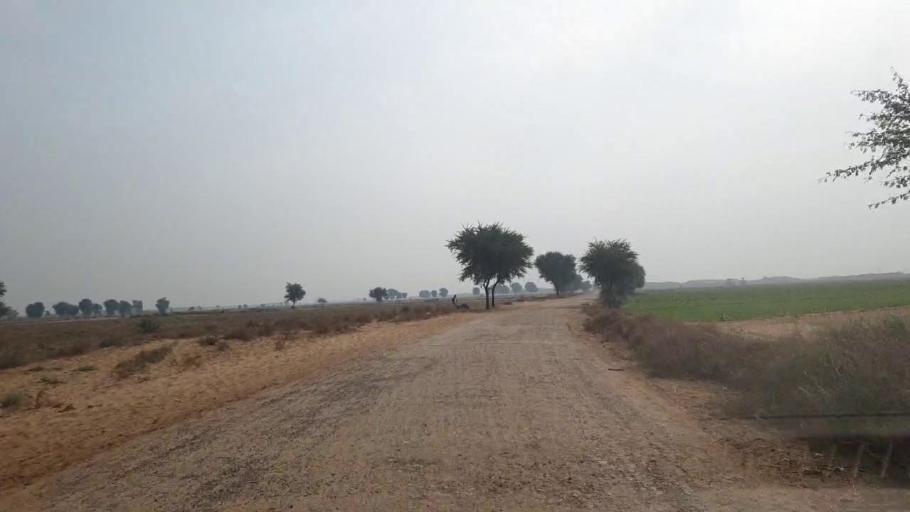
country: PK
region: Sindh
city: Sann
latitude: 26.0244
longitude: 68.1427
